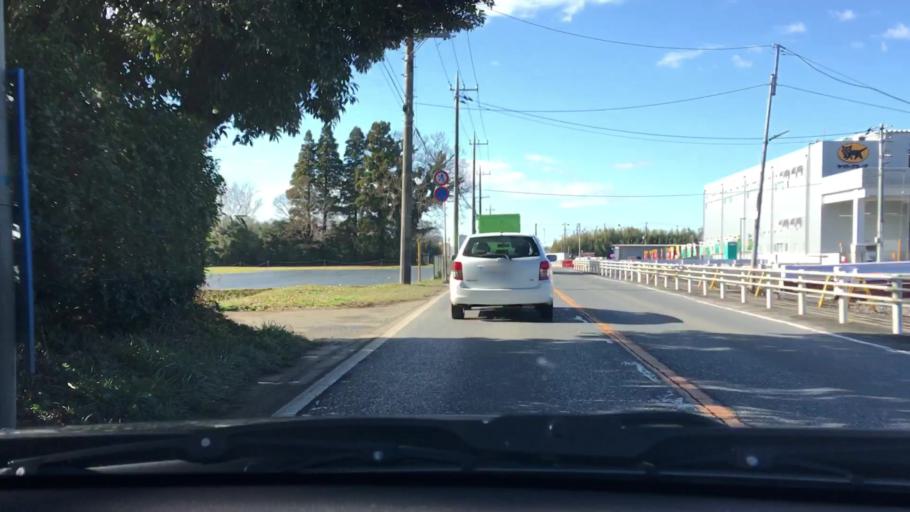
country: JP
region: Chiba
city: Narita
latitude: 35.7868
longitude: 140.4013
